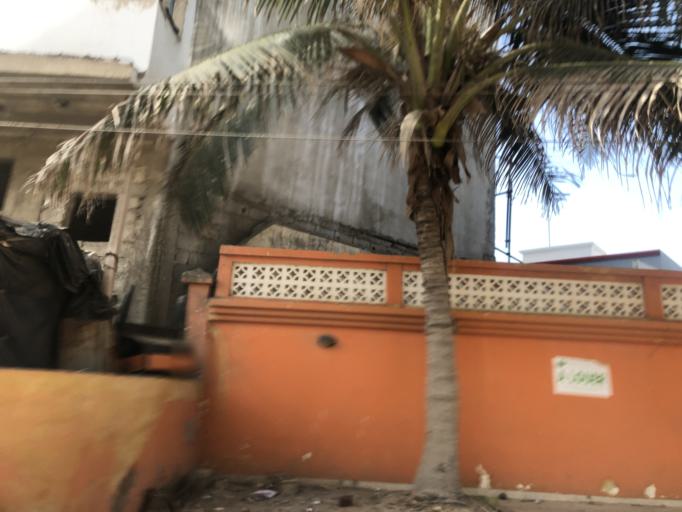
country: SN
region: Dakar
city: Mermoz Boabab
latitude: 14.7555
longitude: -17.4921
